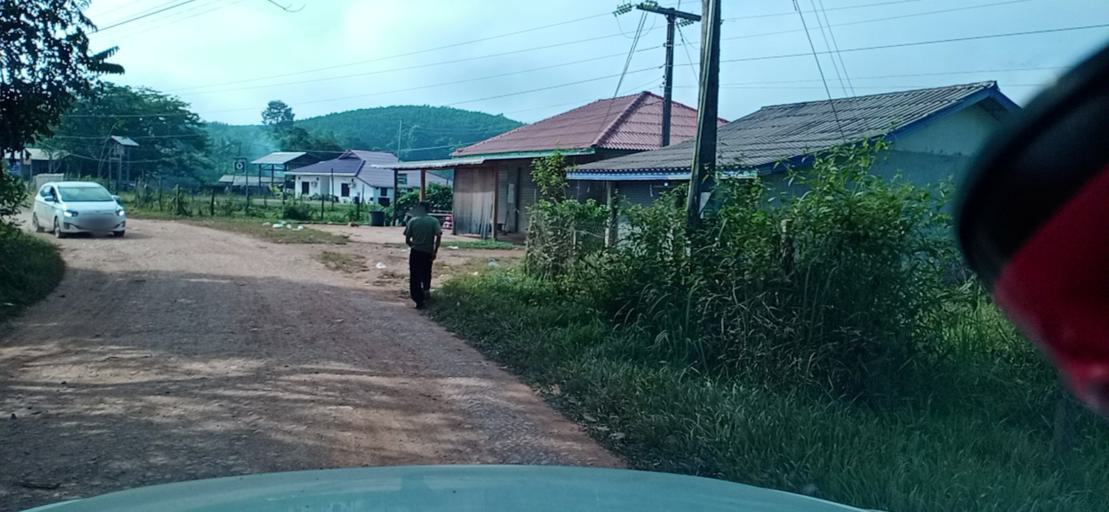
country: TH
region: Changwat Bueng Kan
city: Pak Khat
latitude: 18.6811
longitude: 103.1881
